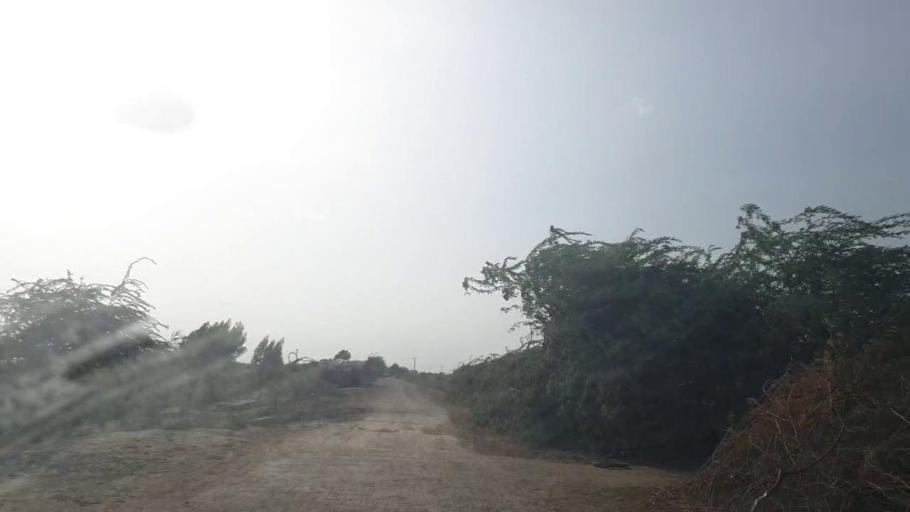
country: PK
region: Sindh
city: Tando Bago
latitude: 24.7640
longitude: 69.0772
